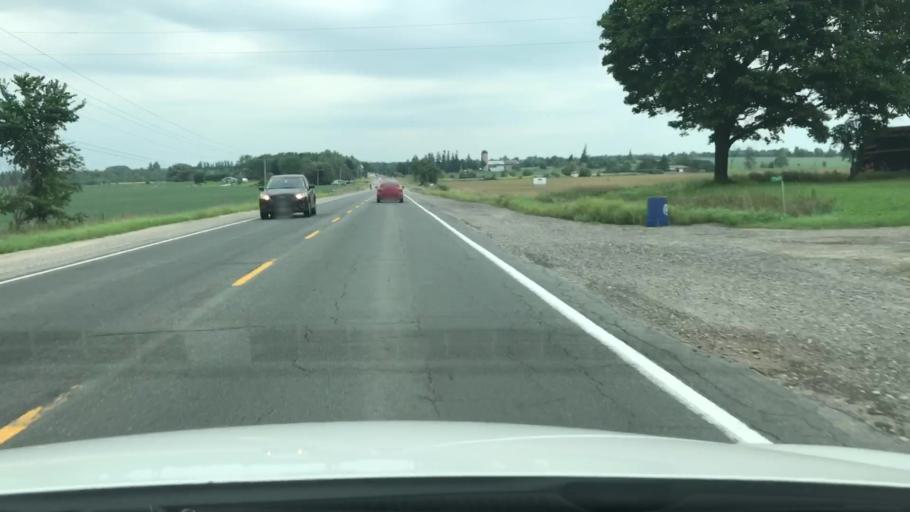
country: CA
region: Ontario
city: Innisfil
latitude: 44.3073
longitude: -79.6150
